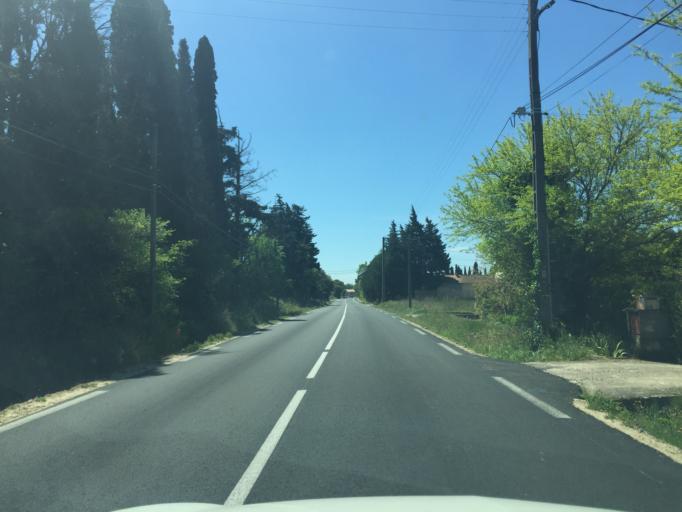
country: FR
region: Provence-Alpes-Cote d'Azur
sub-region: Departement du Vaucluse
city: Orange
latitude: 44.1135
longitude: 4.7943
